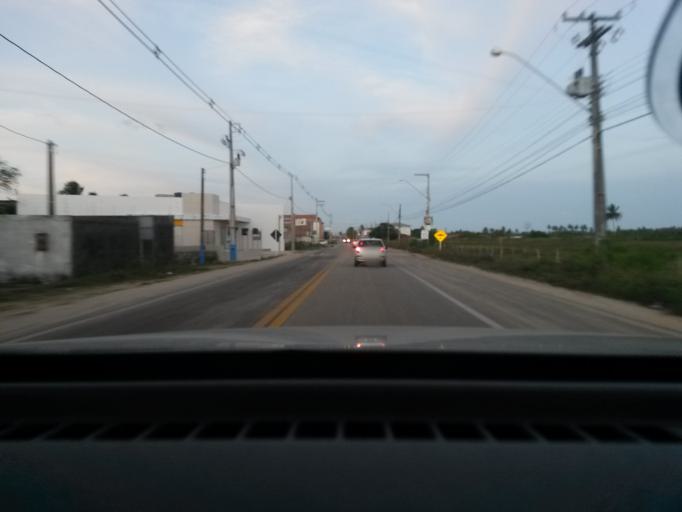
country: BR
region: Sergipe
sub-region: Sao Cristovao
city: Sao Cristovao
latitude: -11.0901
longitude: -37.1352
